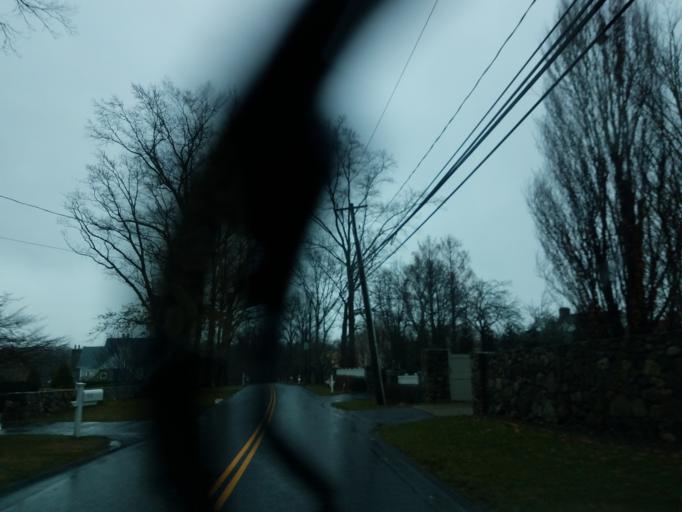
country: US
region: Connecticut
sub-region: Fairfield County
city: Southport
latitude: 41.1310
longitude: -73.3184
